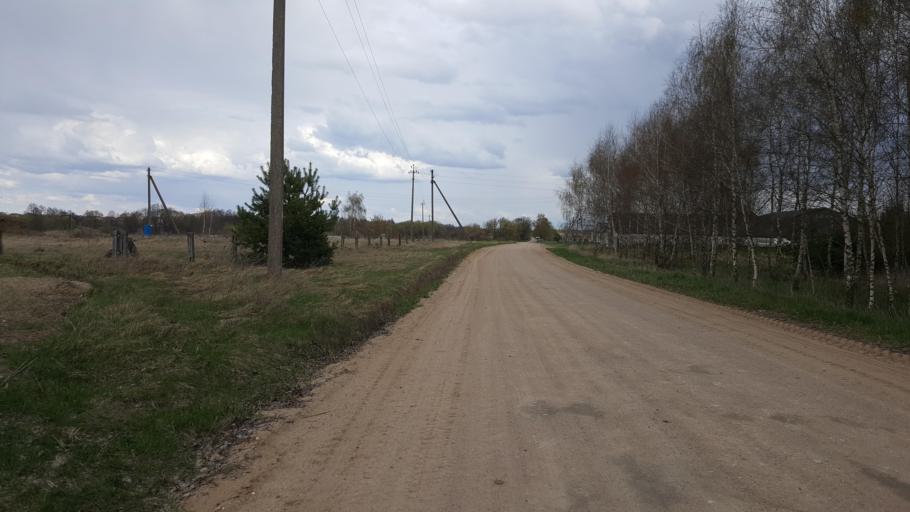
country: BY
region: Brest
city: Kamyanyets
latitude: 52.3954
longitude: 23.7487
